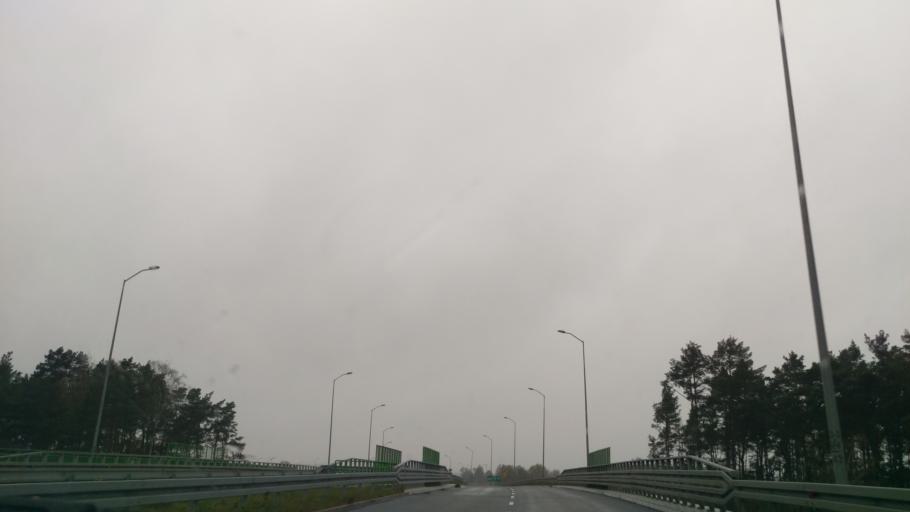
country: PL
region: West Pomeranian Voivodeship
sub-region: Szczecin
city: Szczecin
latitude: 53.4079
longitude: 14.7020
